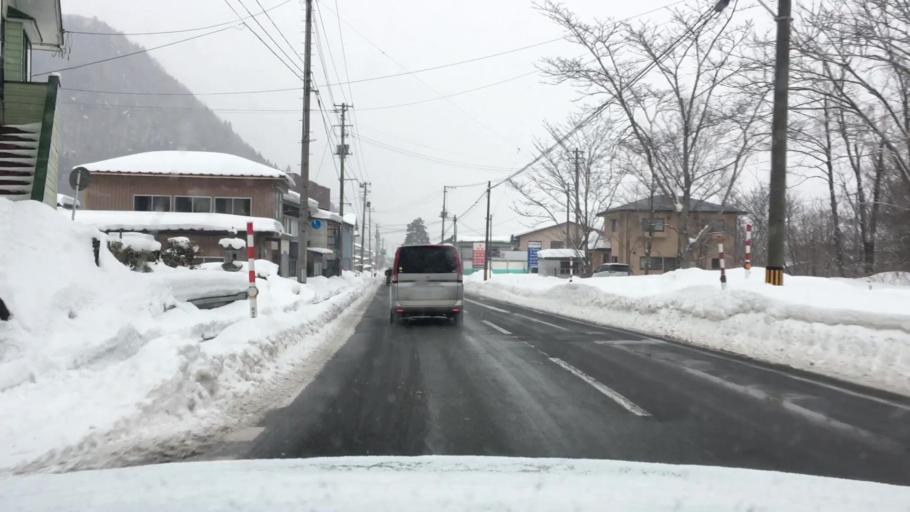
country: JP
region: Iwate
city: Ichinohe
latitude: 40.0911
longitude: 141.0468
